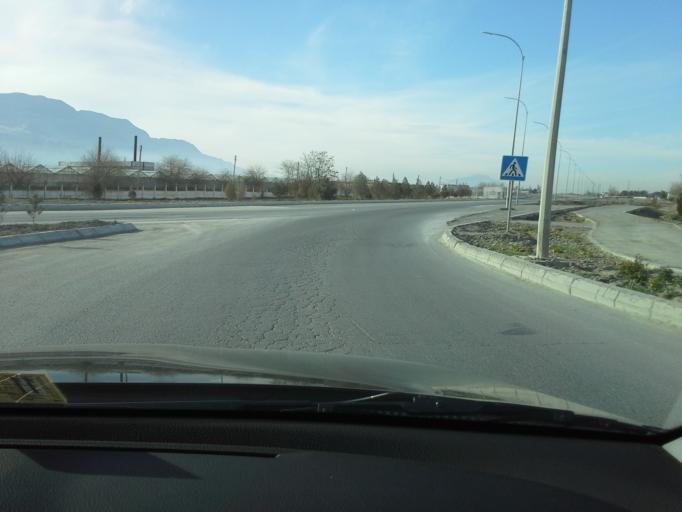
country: TM
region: Ahal
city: Abadan
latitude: 38.0218
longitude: 58.1792
